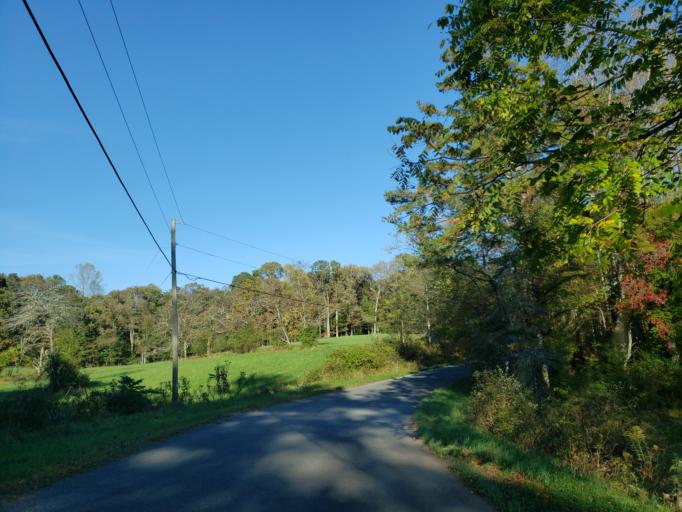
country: US
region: Georgia
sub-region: Gilmer County
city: Ellijay
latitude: 34.6441
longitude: -84.2933
